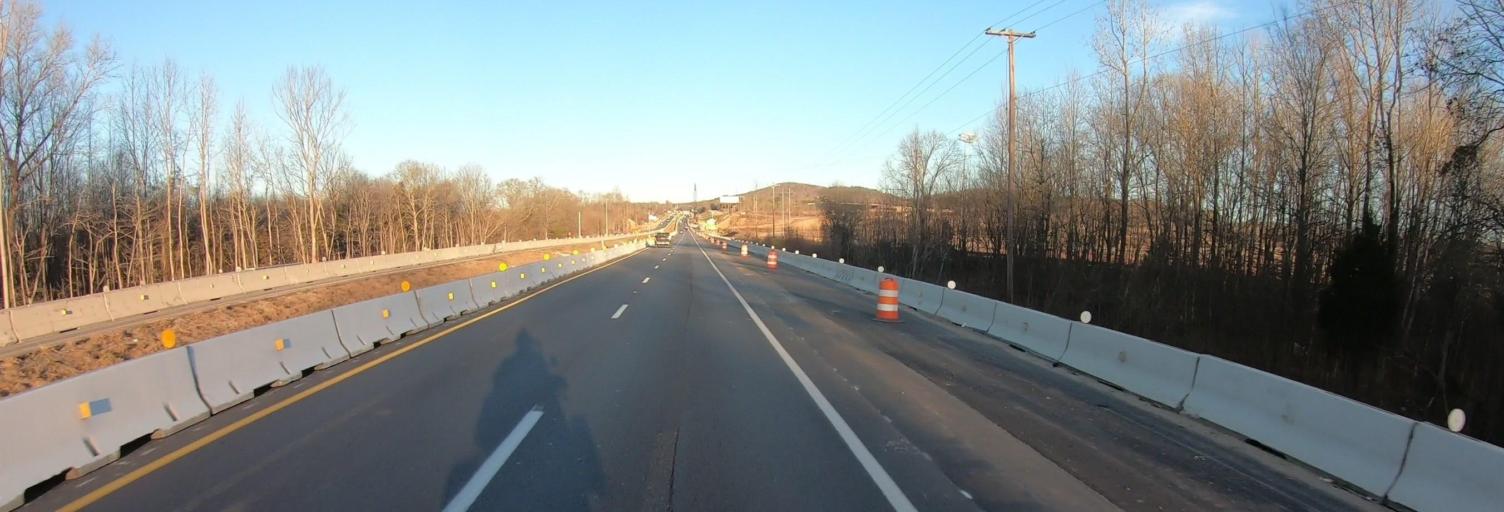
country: US
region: South Carolina
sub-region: Cherokee County
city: Blacksburg
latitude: 35.1321
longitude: -81.5369
